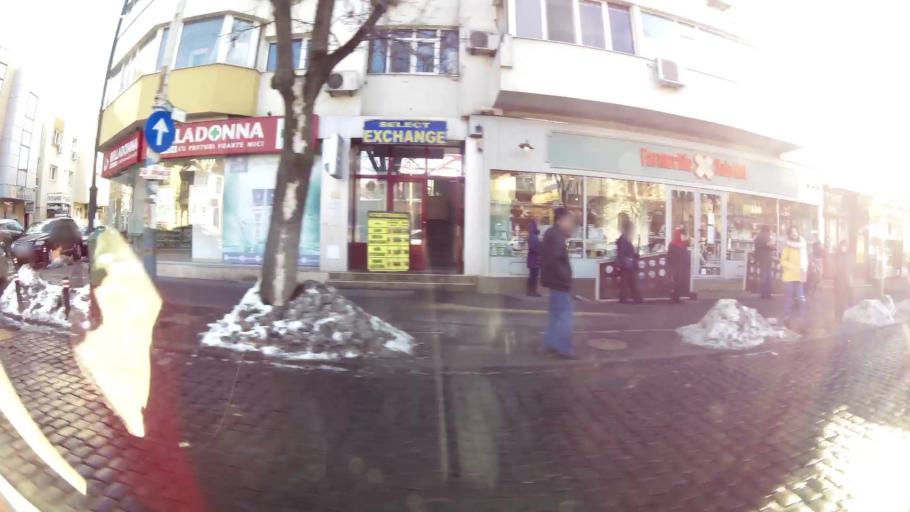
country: RO
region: Bucuresti
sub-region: Municipiul Bucuresti
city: Bucharest
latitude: 44.4618
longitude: 26.0949
